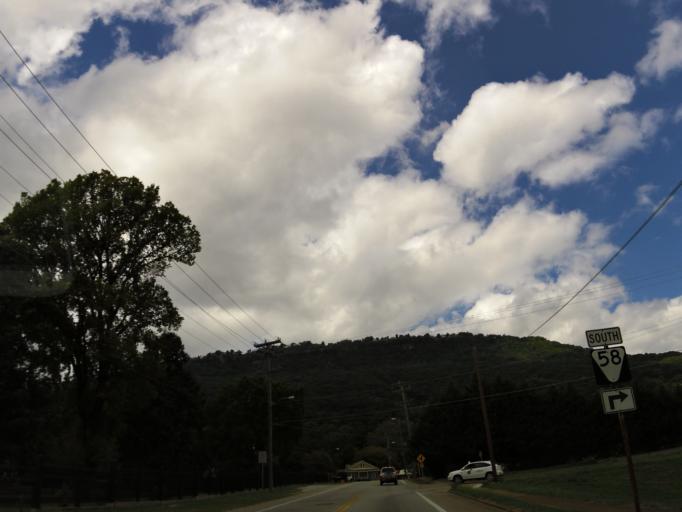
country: US
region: Tennessee
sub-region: Hamilton County
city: Lookout Mountain
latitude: 35.0081
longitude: -85.3258
